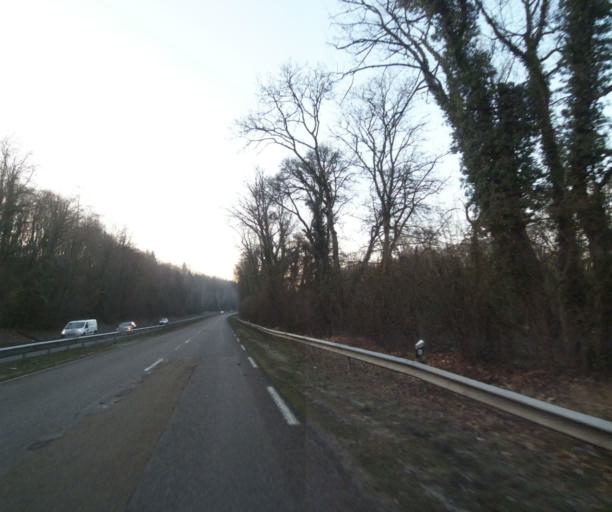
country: FR
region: Lorraine
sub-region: Departement de la Meuse
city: Ancerville
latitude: 48.6109
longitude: 5.0066
